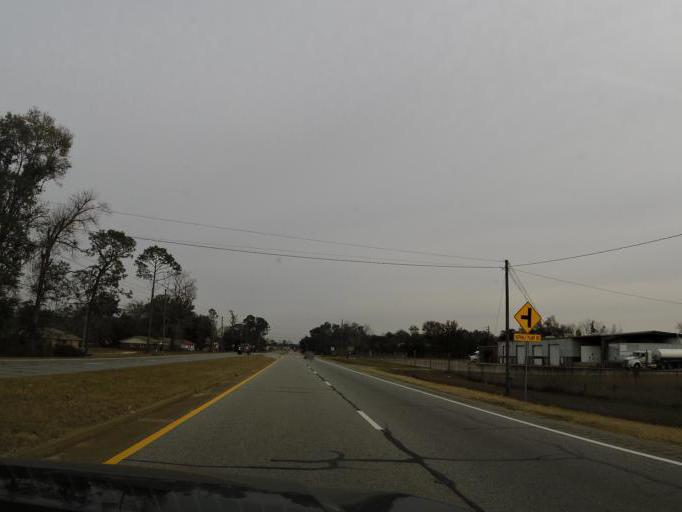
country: US
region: Georgia
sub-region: Decatur County
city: Bainbridge
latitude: 30.9292
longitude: -84.6290
